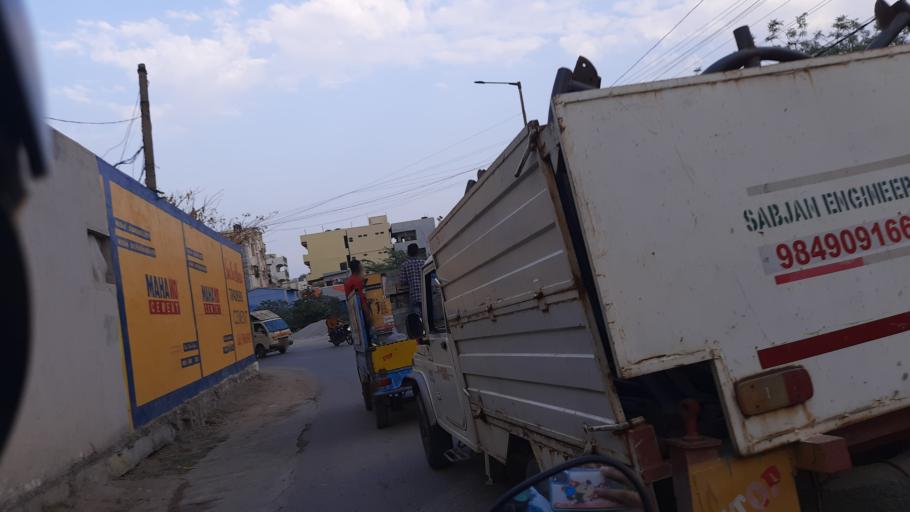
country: IN
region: Telangana
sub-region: Rangareddi
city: Kukatpalli
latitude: 17.4930
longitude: 78.4236
